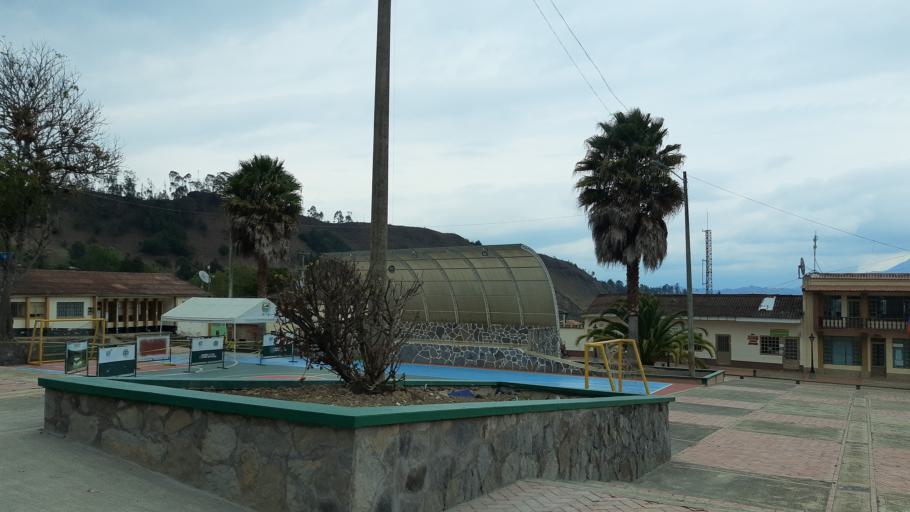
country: CO
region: Boyaca
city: Somondoco
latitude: 4.9710
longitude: -73.3787
